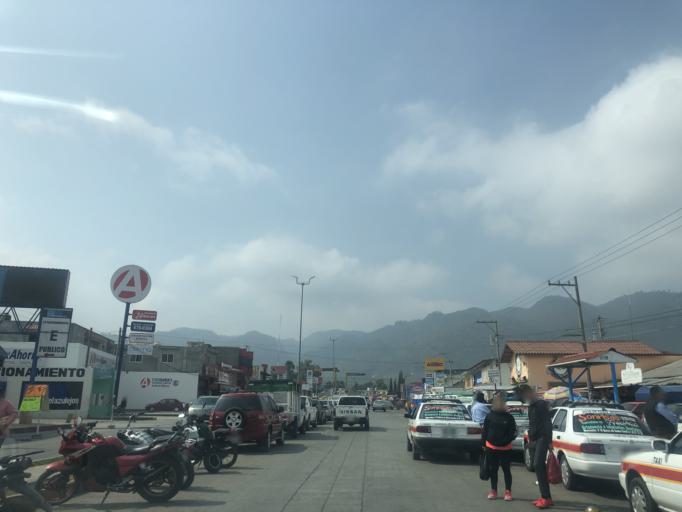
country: MX
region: Chiapas
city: San Cristobal de las Casas
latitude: 16.7195
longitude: -92.6370
